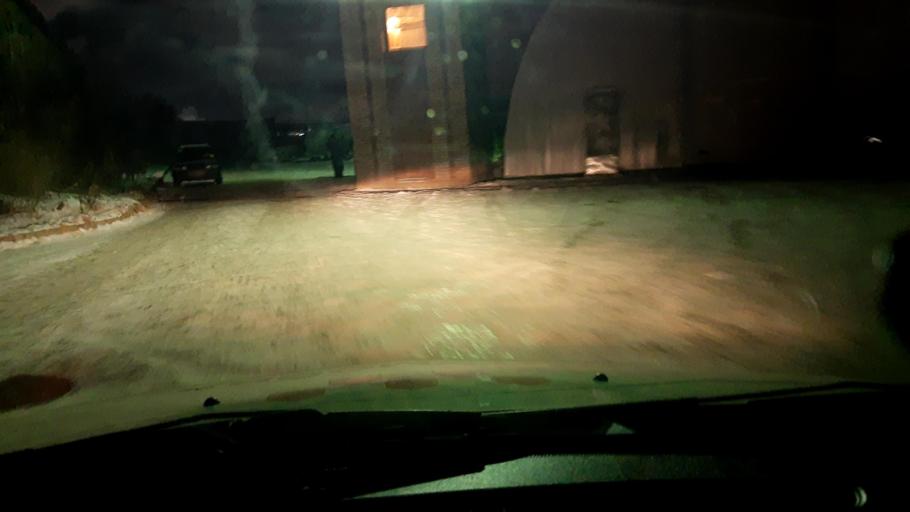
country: RU
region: Bashkortostan
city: Iglino
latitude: 54.7663
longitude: 56.2412
